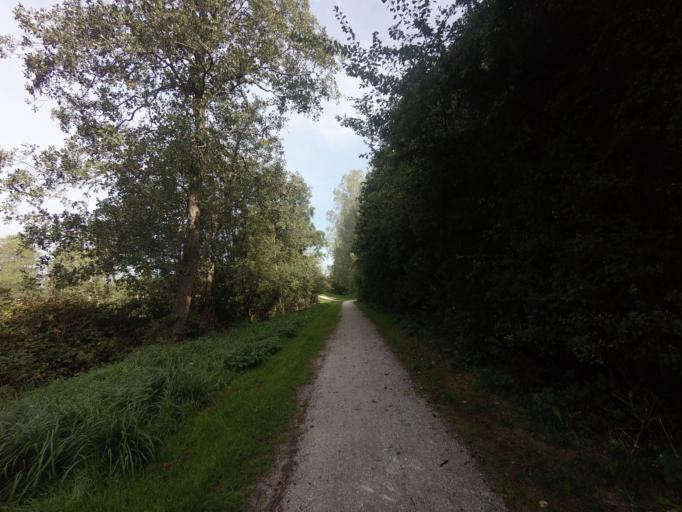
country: NL
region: Groningen
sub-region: Gemeente Zuidhorn
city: Grijpskerk
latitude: 53.2170
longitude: 6.3369
